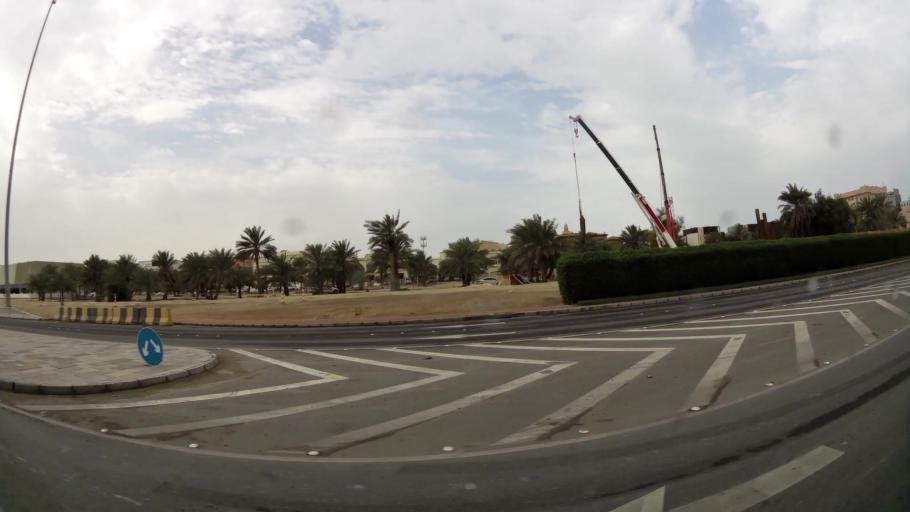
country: AE
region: Abu Dhabi
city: Abu Dhabi
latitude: 24.4774
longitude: 54.3885
